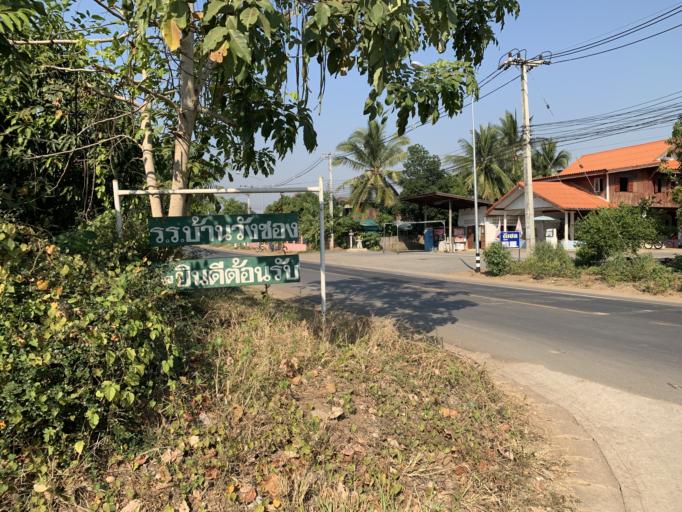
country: TH
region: Phetchabun
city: Phetchabun
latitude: 16.5508
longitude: 101.2122
